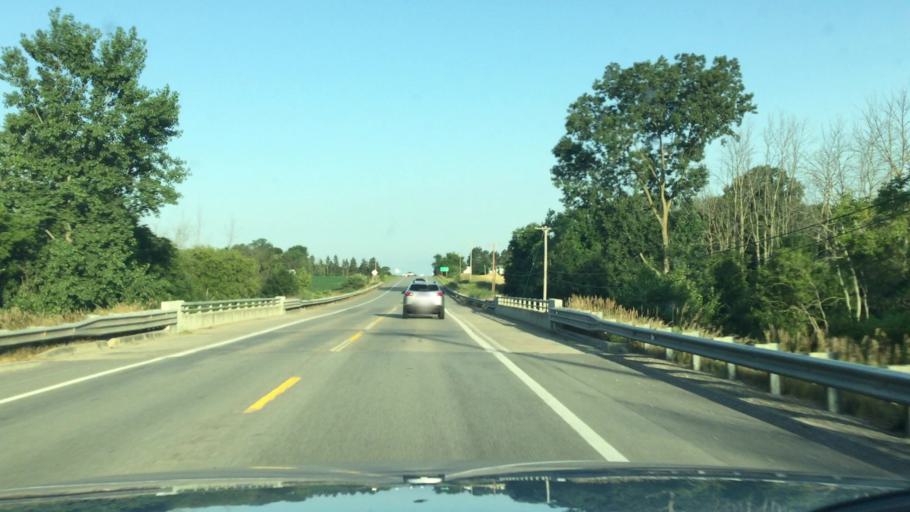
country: US
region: Michigan
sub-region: Gratiot County
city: Ithaca
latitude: 43.1761
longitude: -84.6725
